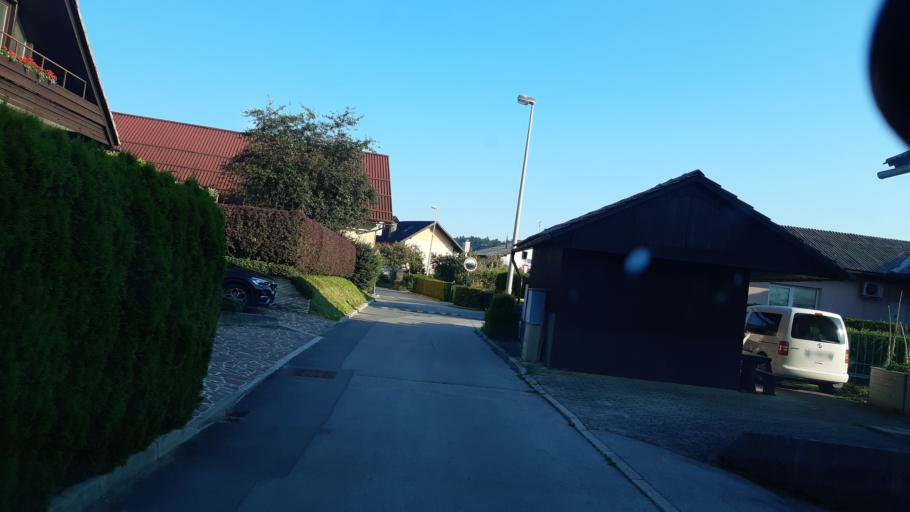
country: SI
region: Medvode
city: Medvode
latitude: 46.1449
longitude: 14.4036
